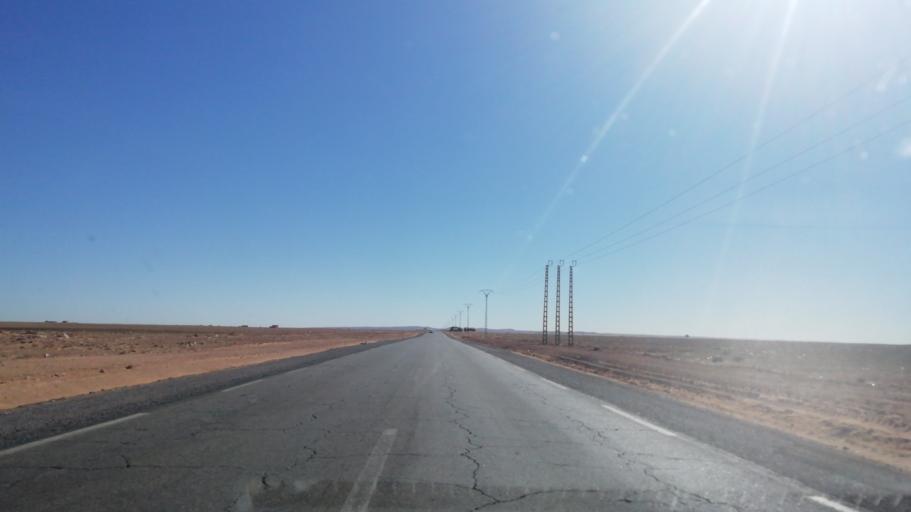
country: DZ
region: Saida
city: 'Ain el Hadjar
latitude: 34.0168
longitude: 0.1094
